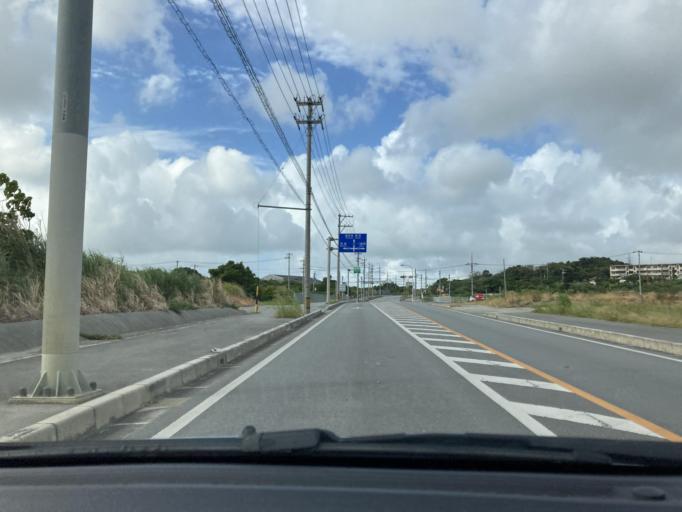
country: JP
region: Okinawa
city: Itoman
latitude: 26.1167
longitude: 127.6919
